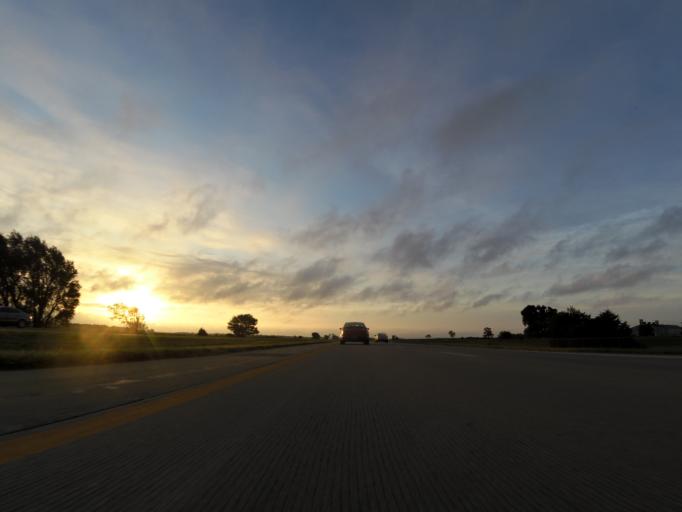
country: US
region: Kansas
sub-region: Reno County
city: Haven
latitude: 37.9104
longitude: -97.8097
